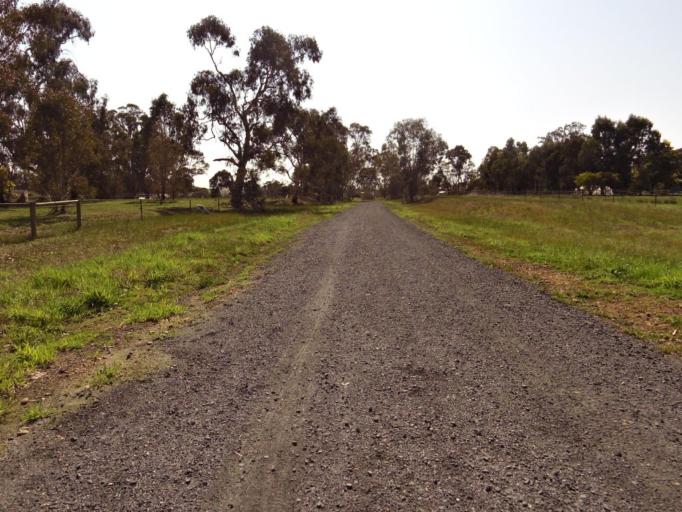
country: AU
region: Victoria
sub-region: Murrindindi
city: Alexandra
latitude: -37.1038
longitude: 145.6173
